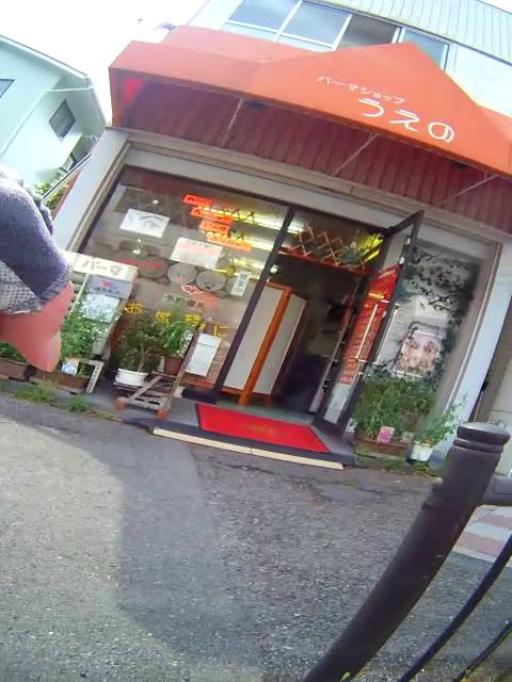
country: JP
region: Osaka
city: Toyonaka
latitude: 34.7949
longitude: 135.4727
